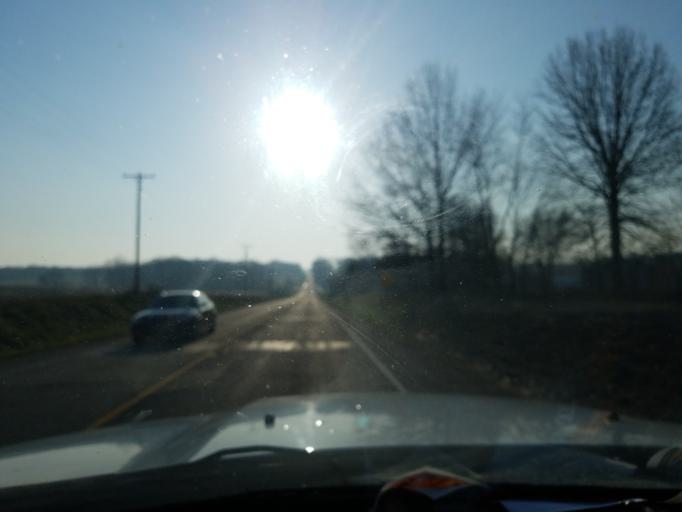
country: US
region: Indiana
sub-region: Vigo County
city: Seelyville
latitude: 39.3901
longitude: -87.2355
